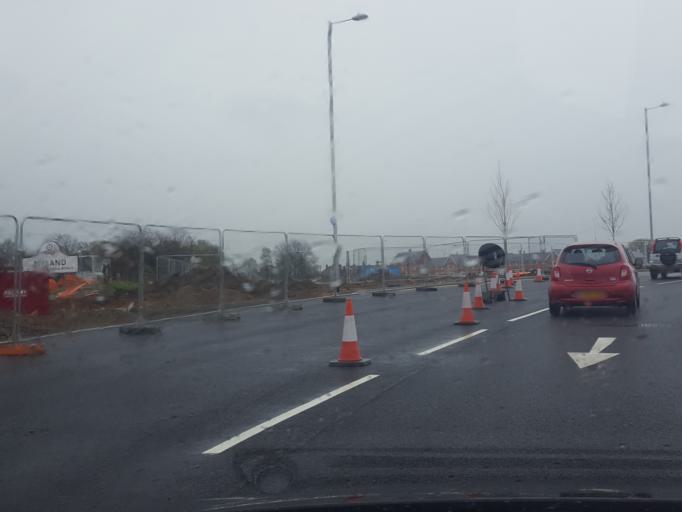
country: GB
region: England
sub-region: Essex
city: Great Horkesley
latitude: 51.9196
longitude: 0.8880
